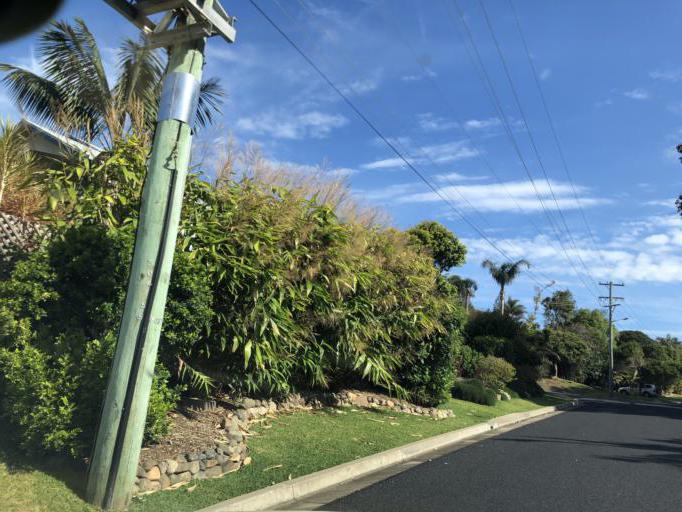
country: AU
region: New South Wales
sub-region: Coffs Harbour
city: Moonee Beach
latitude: -30.2320
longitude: 153.1515
